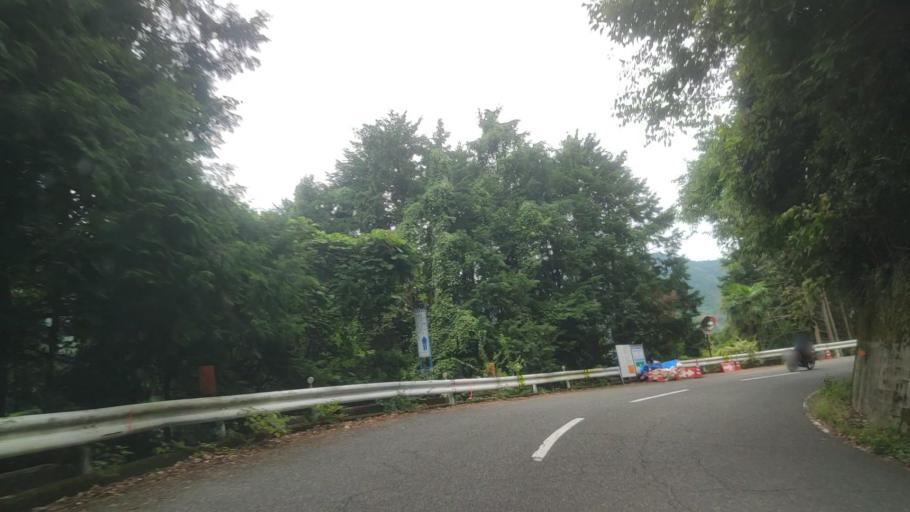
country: JP
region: Wakayama
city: Koya
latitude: 34.2260
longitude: 135.5409
